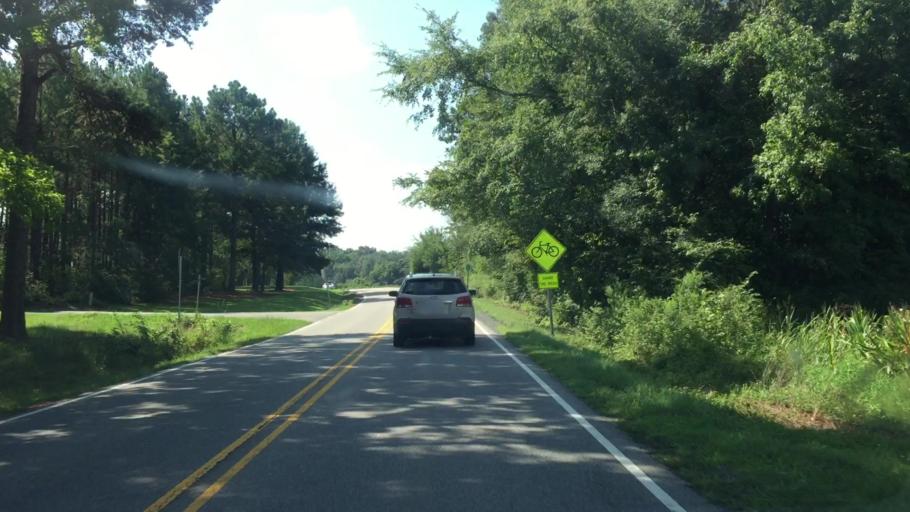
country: US
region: North Carolina
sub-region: Anson County
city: Burnsville
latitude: 35.0686
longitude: -80.2838
